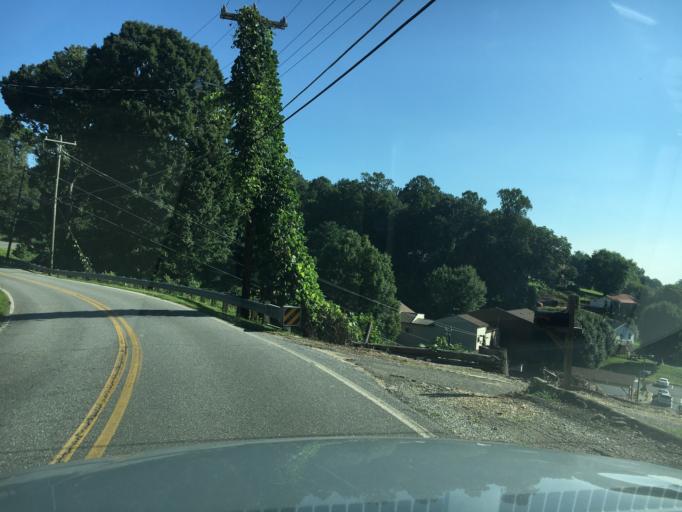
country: US
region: North Carolina
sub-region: McDowell County
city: Marion
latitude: 35.6807
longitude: -82.0184
